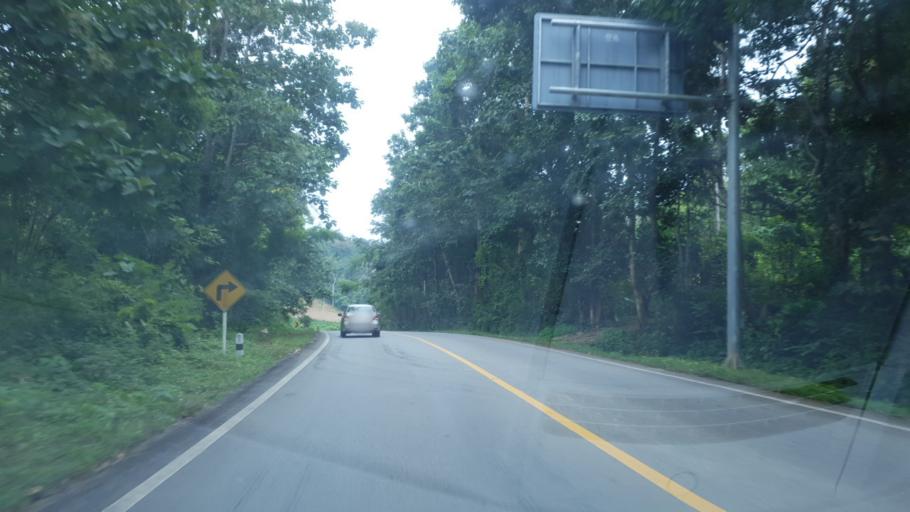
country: TH
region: Mae Hong Son
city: Khun Yuam
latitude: 18.7129
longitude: 97.9108
